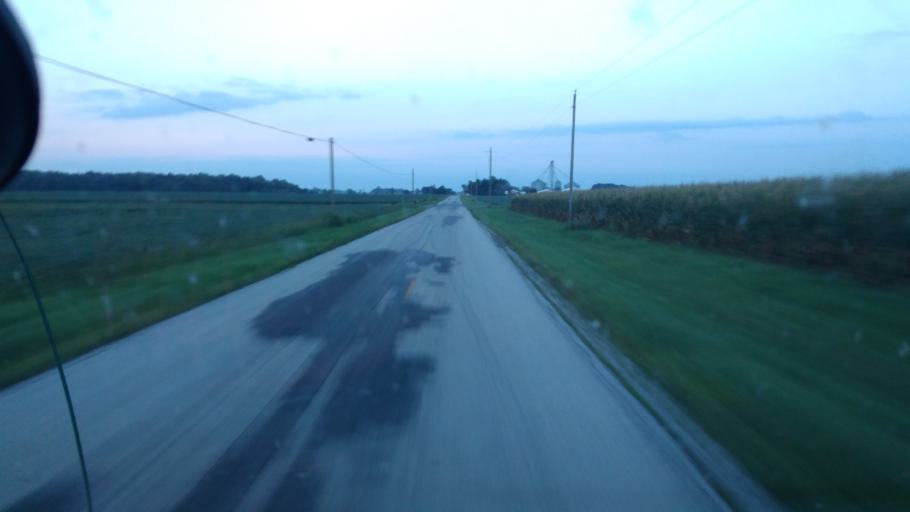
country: US
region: Ohio
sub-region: Hardin County
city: Kenton
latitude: 40.6722
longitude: -83.4972
